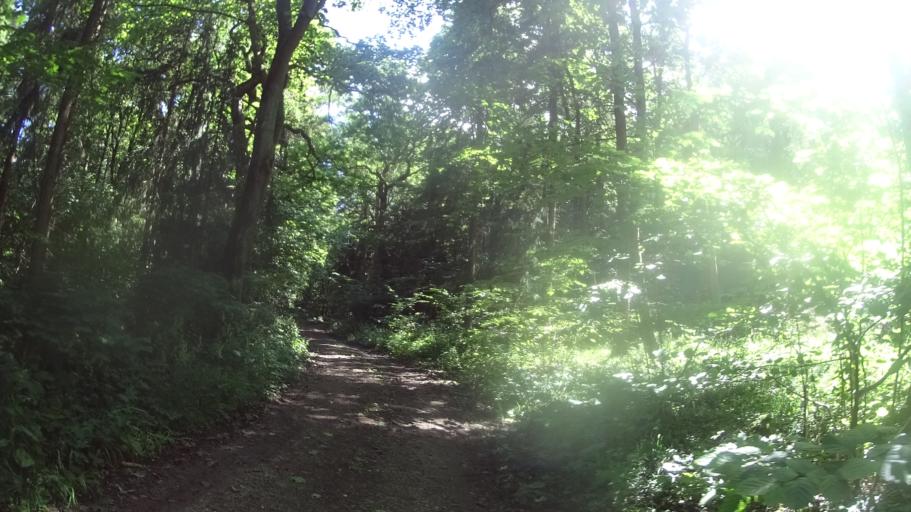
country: DE
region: Lower Saxony
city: Elbe
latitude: 52.1085
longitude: 10.2973
